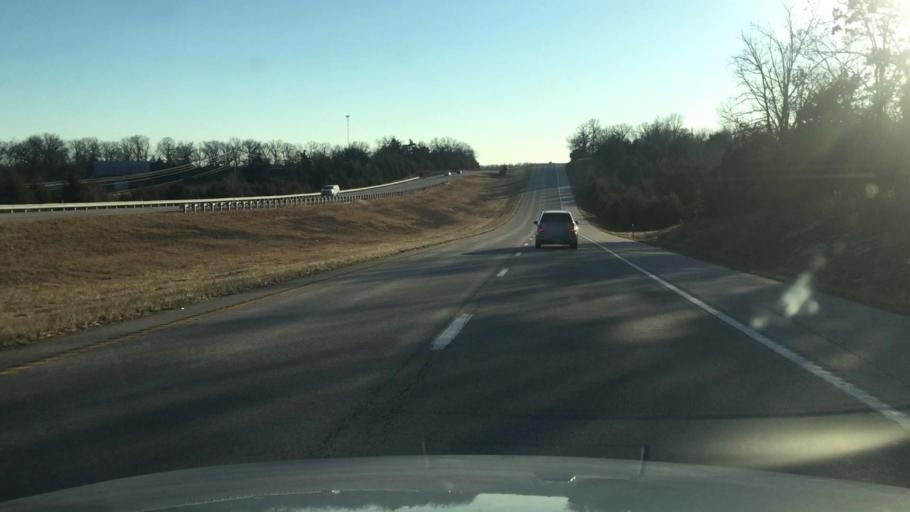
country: US
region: Missouri
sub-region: Cole County
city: Wardsville
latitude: 38.4583
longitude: -92.2976
